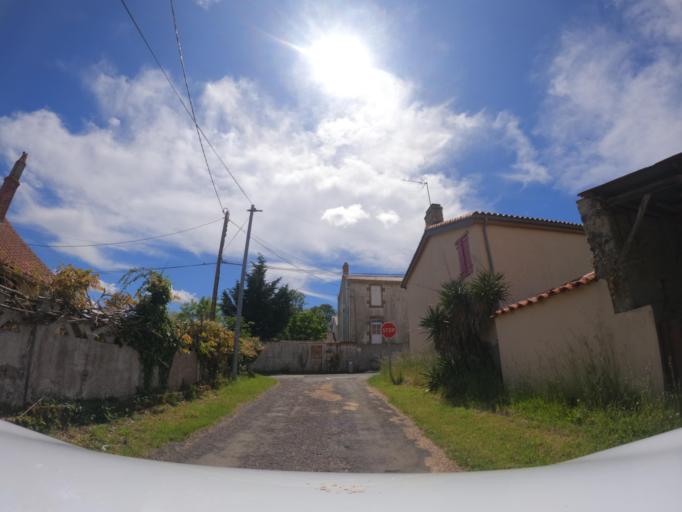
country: FR
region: Pays de la Loire
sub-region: Departement de la Vendee
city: Le Champ-Saint-Pere
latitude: 46.4914
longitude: -1.3353
